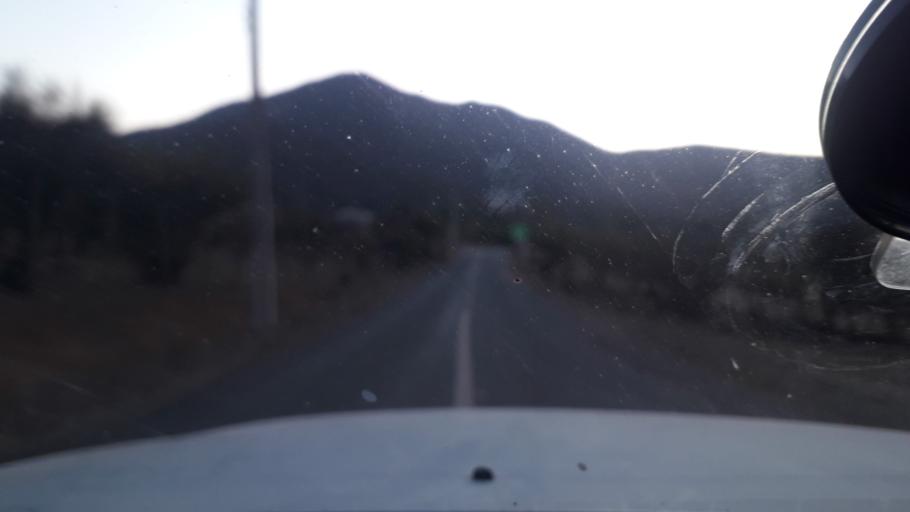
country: CL
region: Valparaiso
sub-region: Provincia de Marga Marga
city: Limache
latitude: -33.1769
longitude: -71.1232
